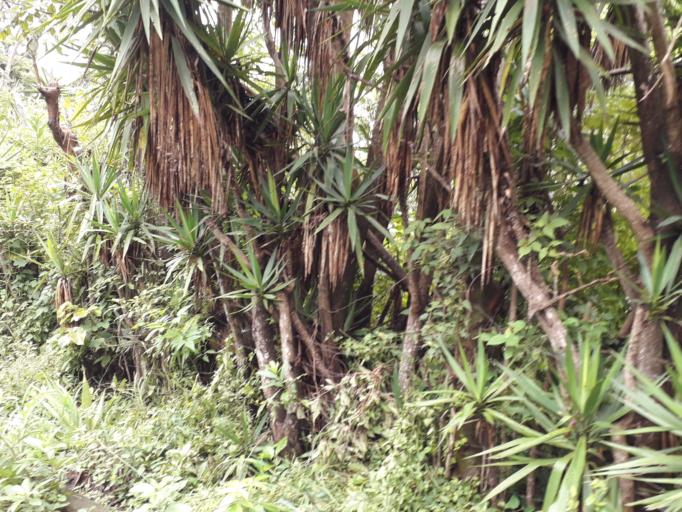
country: GT
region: Escuintla
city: Guanagazapa
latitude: 14.3139
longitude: -90.5596
